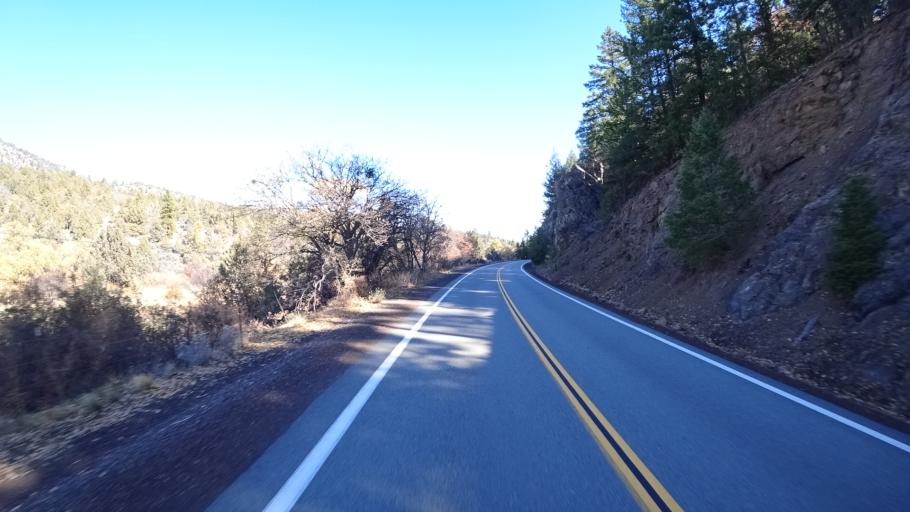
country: US
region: California
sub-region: Siskiyou County
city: Weed
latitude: 41.4629
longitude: -122.6202
